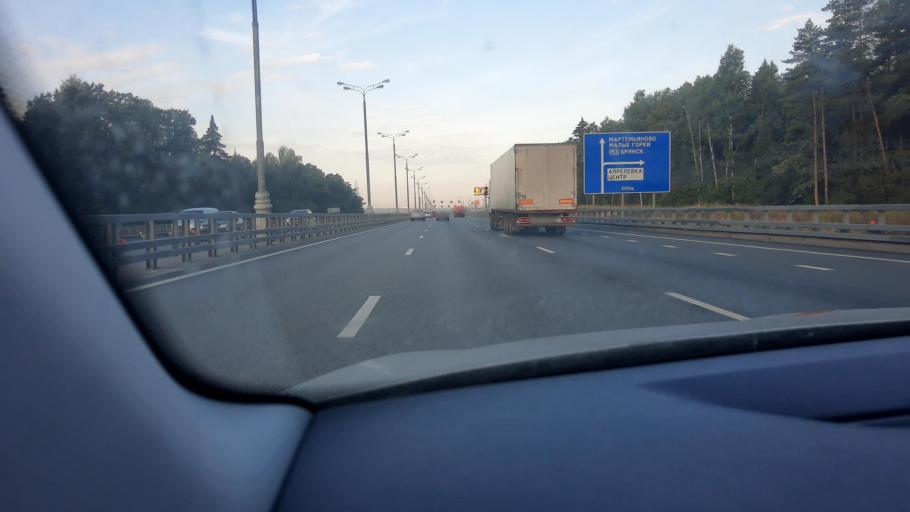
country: RU
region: Moskovskaya
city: Aprelevka
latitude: 55.5432
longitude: 37.0963
